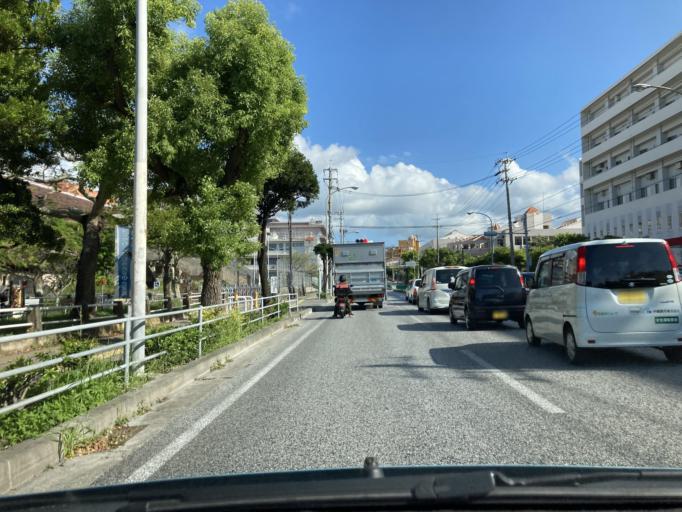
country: JP
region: Okinawa
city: Naha-shi
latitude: 26.2076
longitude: 127.6925
